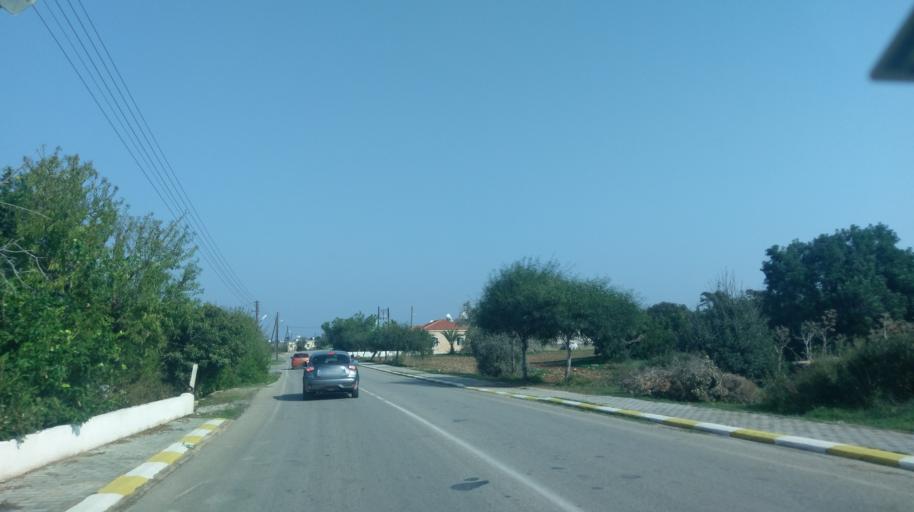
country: CY
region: Ammochostos
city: Leonarisso
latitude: 35.5261
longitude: 34.1798
